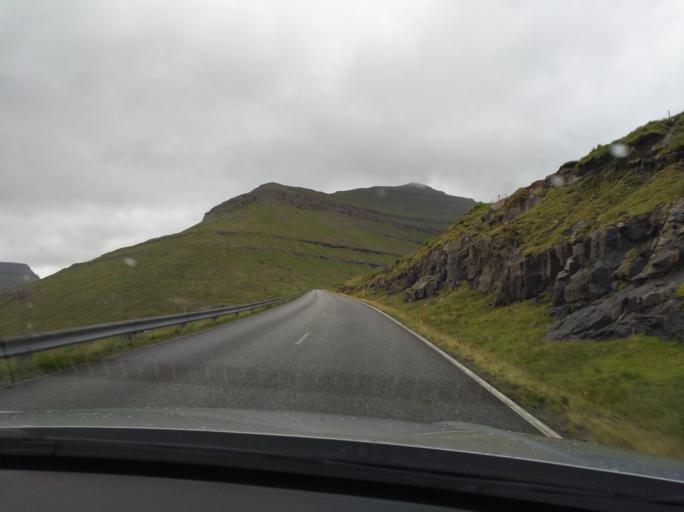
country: FO
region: Eysturoy
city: Fuglafjordur
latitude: 62.2213
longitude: -6.8729
